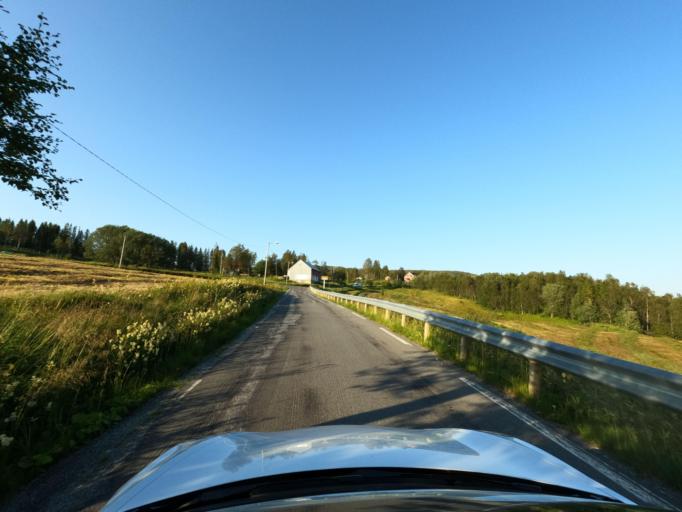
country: NO
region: Nordland
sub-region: Ballangen
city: Ballangen
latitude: 68.4935
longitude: 16.7365
